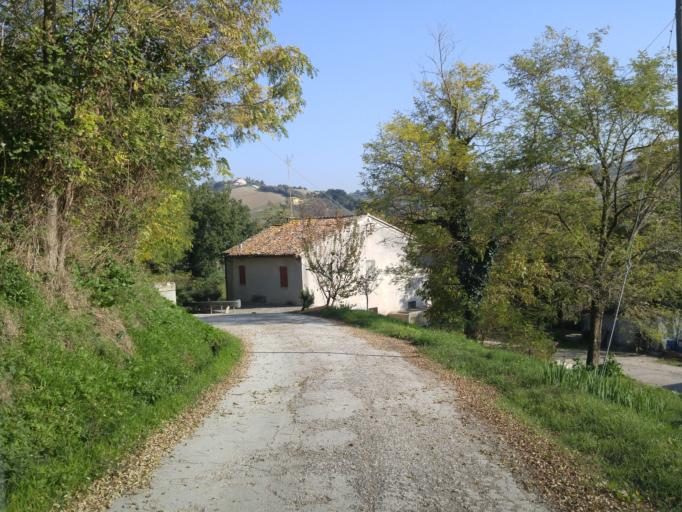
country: IT
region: The Marches
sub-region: Provincia di Pesaro e Urbino
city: Montemaggiore al Metauro
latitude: 43.7358
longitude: 12.9509
